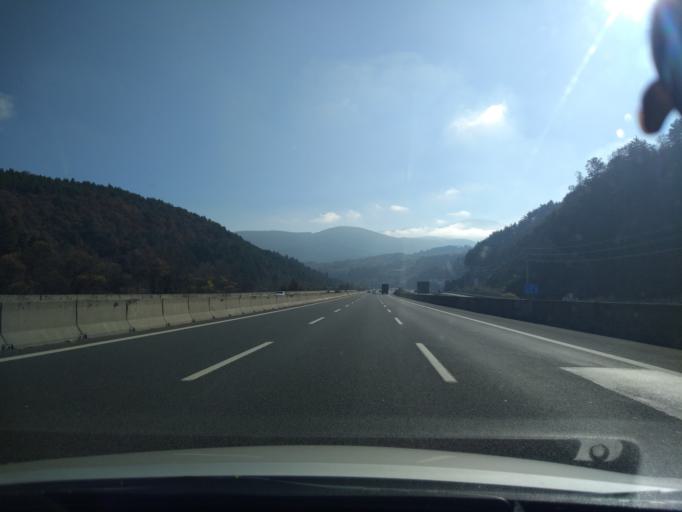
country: TR
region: Bolu
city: Bolu
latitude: 40.7493
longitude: 31.7792
